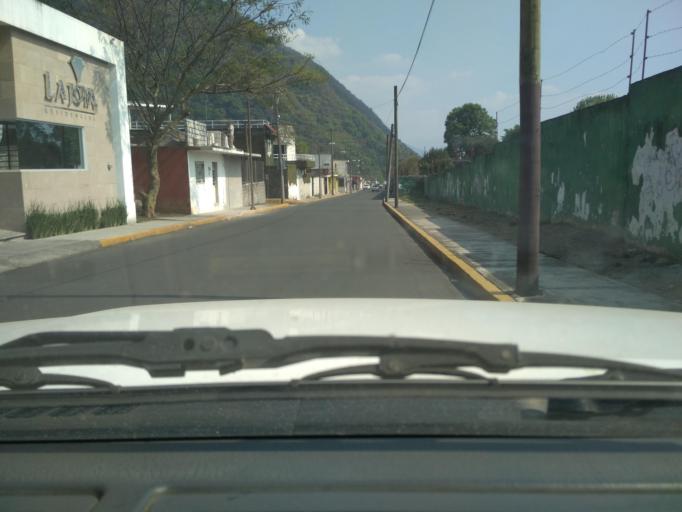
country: MX
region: Veracruz
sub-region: Mariano Escobedo
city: Palmira
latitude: 18.8721
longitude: -97.0967
